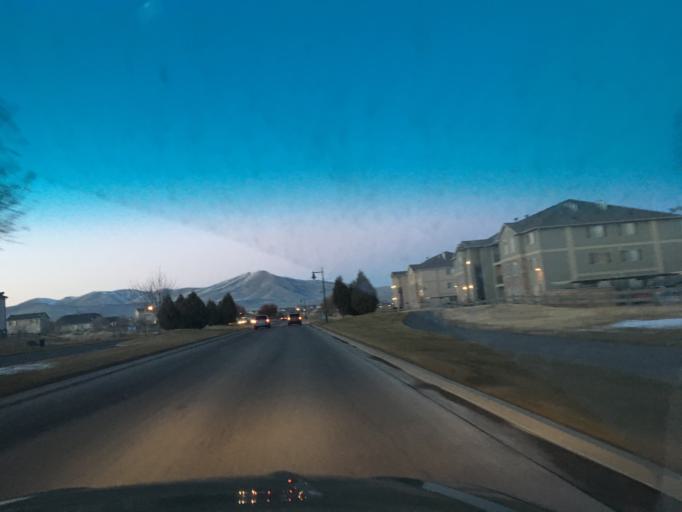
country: US
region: Utah
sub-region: Utah County
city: Eagle Mountain
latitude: 40.3643
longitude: -111.9764
